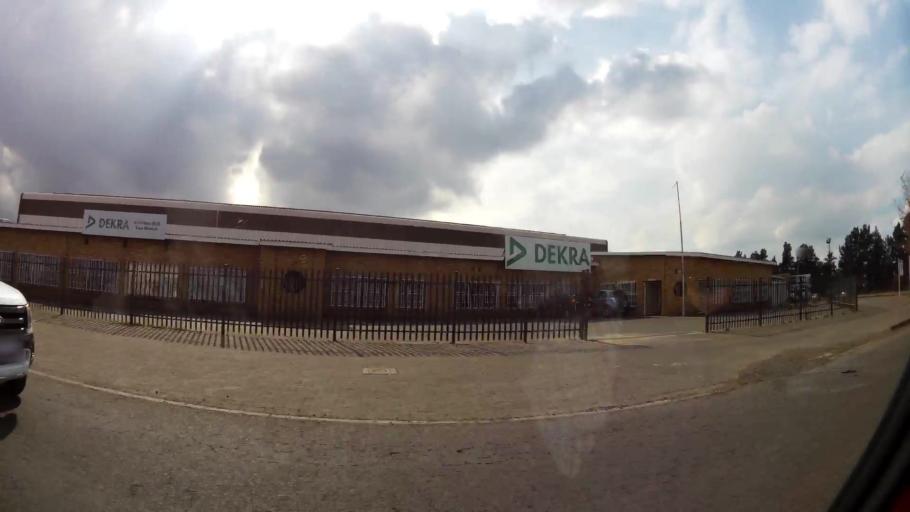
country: ZA
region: Gauteng
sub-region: Sedibeng District Municipality
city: Vanderbijlpark
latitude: -26.7036
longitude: 27.8587
